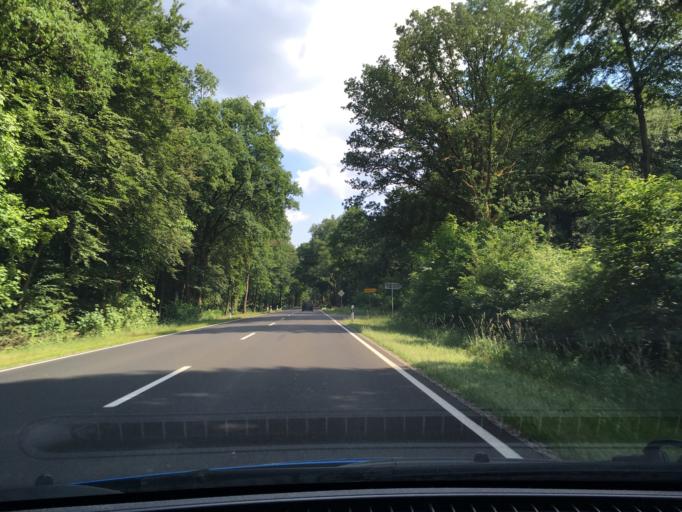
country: DE
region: Lower Saxony
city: Welle
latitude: 53.2133
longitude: 9.8178
